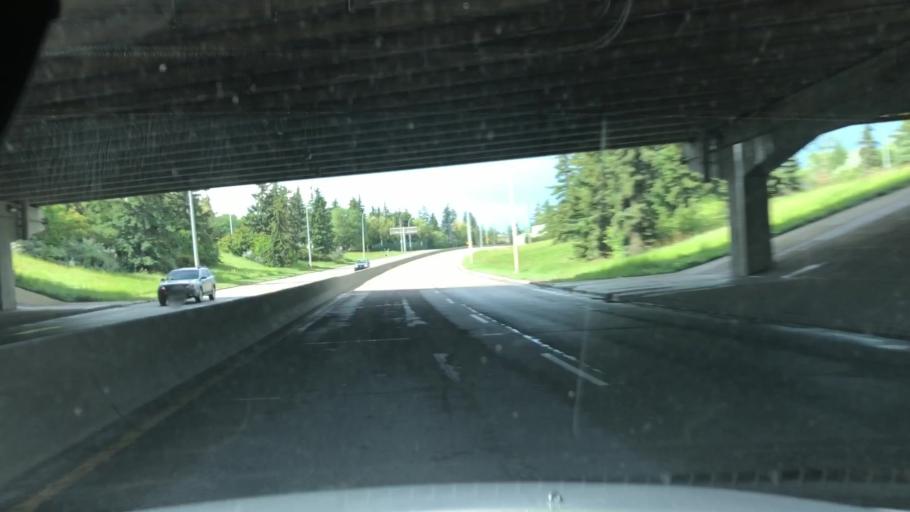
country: CA
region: Alberta
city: Edmonton
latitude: 53.5509
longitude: -113.5497
